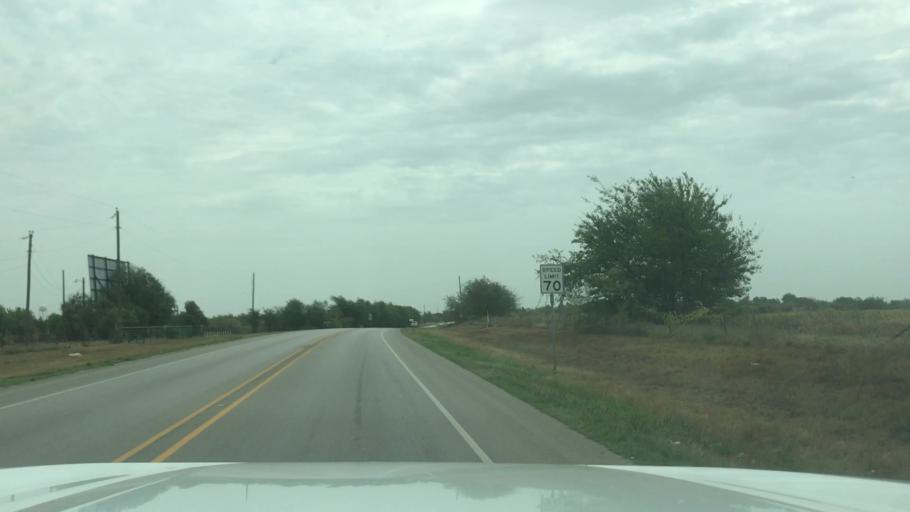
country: US
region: Texas
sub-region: Erath County
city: Dublin
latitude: 32.0922
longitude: -98.3651
